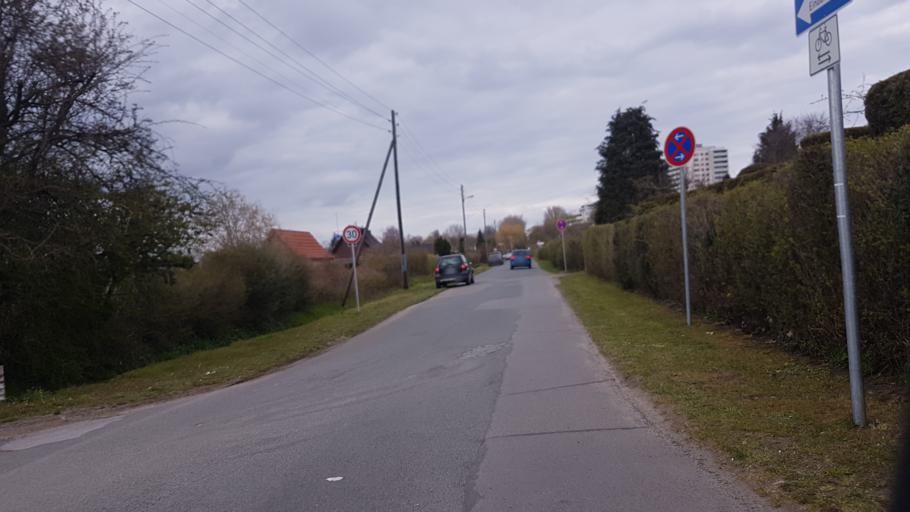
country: DE
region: Lower Saxony
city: Hannover
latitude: 52.4080
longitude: 9.7461
